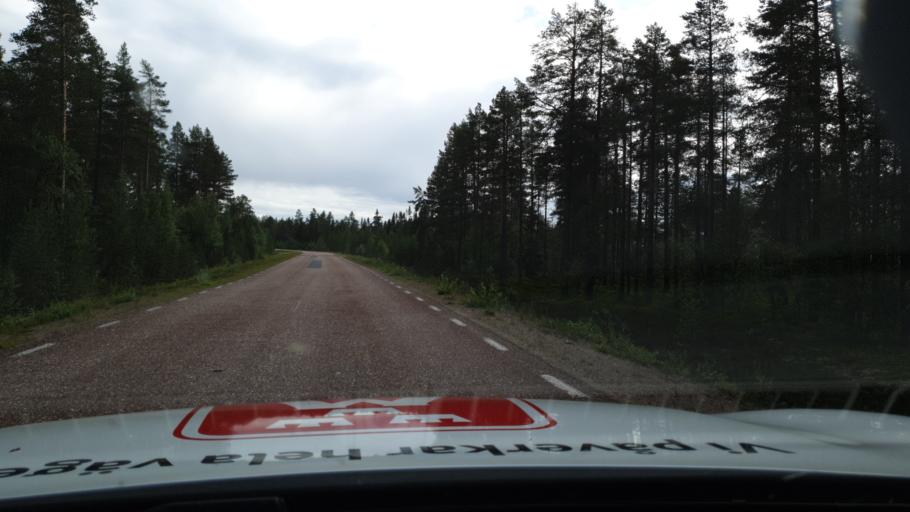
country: SE
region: Dalarna
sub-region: Alvdalens Kommun
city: AElvdalen
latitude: 61.7777
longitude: 13.4819
